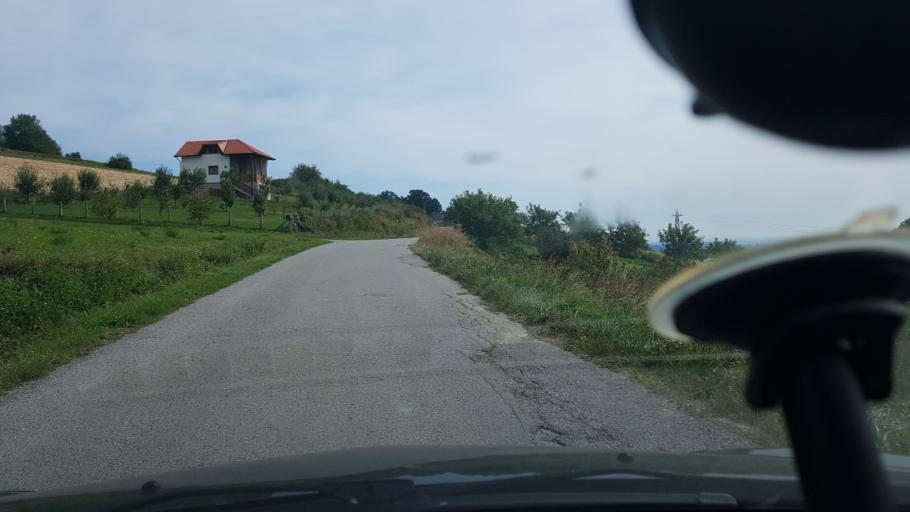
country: HR
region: Varazdinska
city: Ljubescica
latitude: 46.1243
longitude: 16.4528
